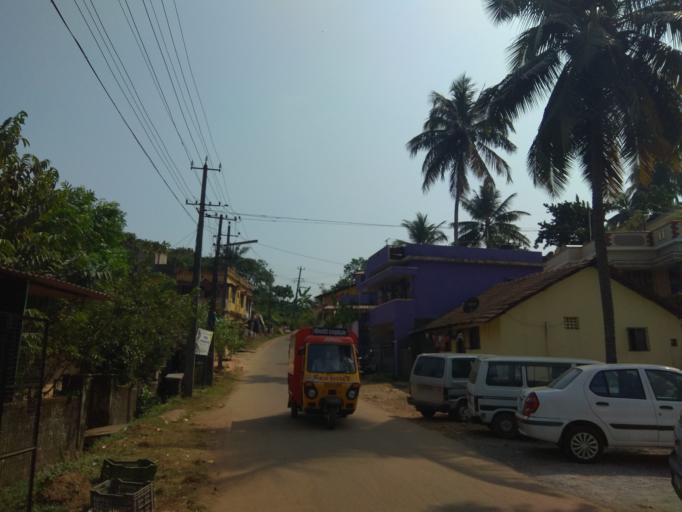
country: IN
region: Karnataka
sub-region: Dakshina Kannada
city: Mangalore
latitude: 12.9274
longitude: 74.8435
